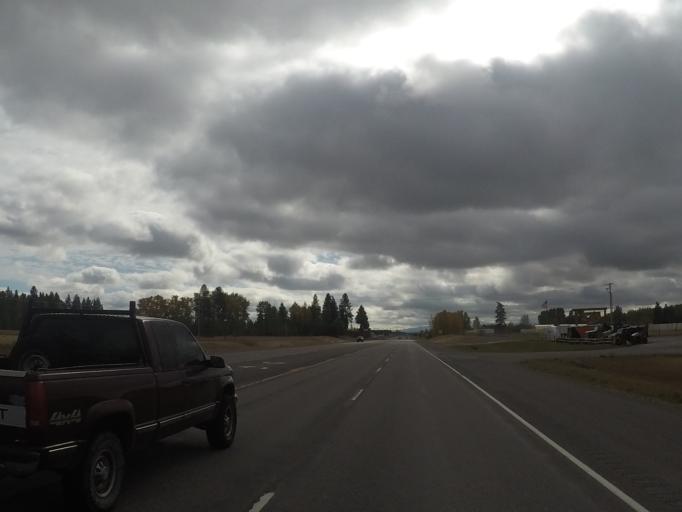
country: US
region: Montana
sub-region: Flathead County
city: Columbia Falls
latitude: 48.3609
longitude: -114.2411
